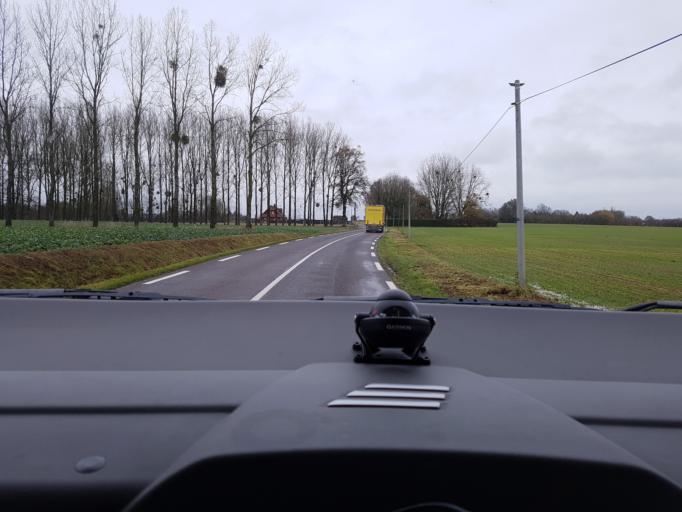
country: FR
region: Haute-Normandie
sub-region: Departement de la Seine-Maritime
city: Gournay-en-Bray
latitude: 49.4390
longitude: 1.6546
